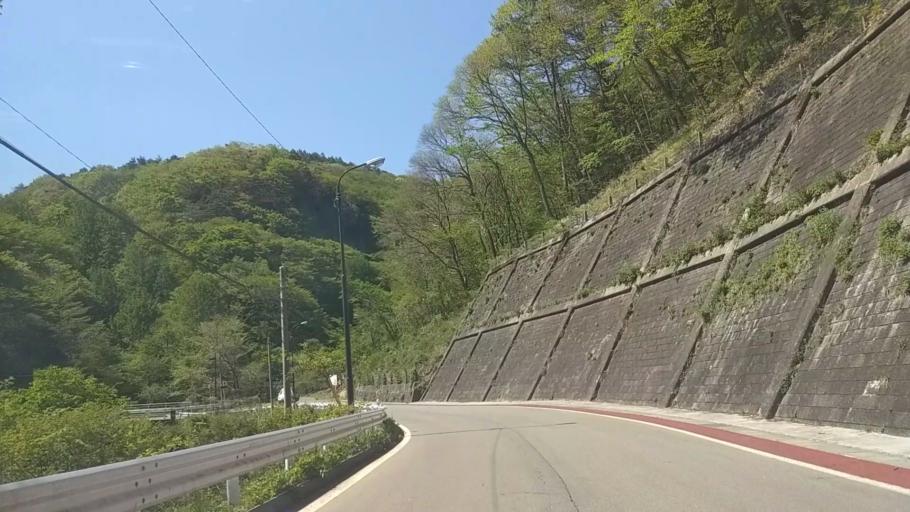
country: JP
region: Yamanashi
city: Nirasaki
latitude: 35.9208
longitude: 138.4453
